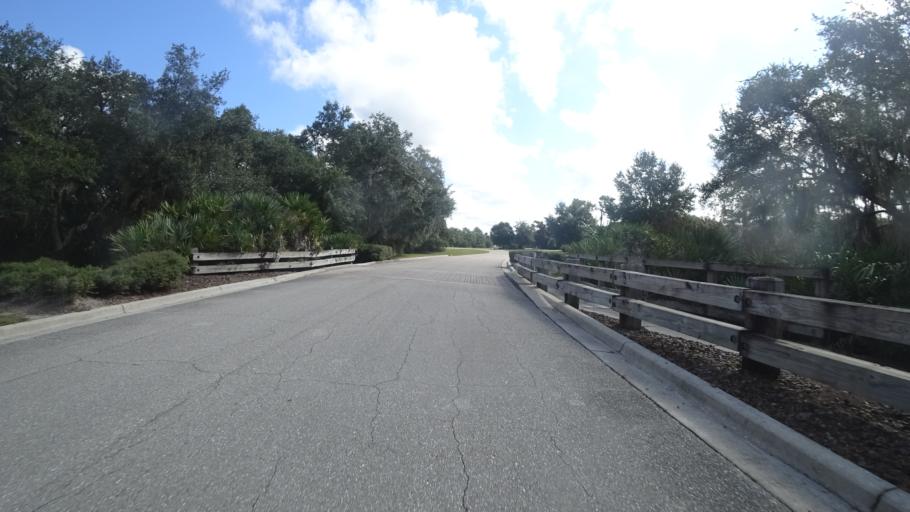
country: US
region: Florida
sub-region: Sarasota County
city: Fruitville
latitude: 27.3901
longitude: -82.3063
